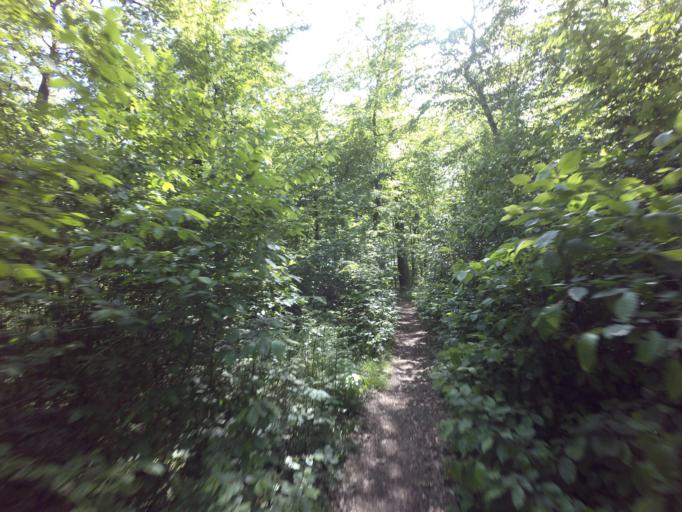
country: DE
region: Lower Saxony
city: Cremlingen
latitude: 52.2934
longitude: 10.6367
